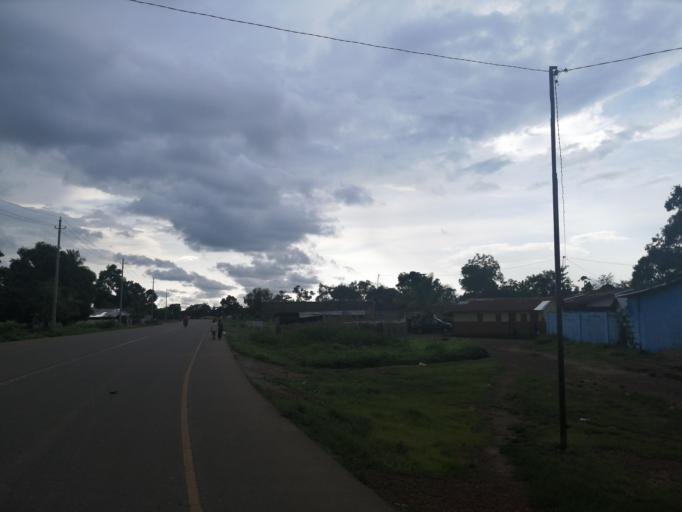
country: SL
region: Northern Province
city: Port Loko
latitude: 8.7745
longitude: -12.7880
